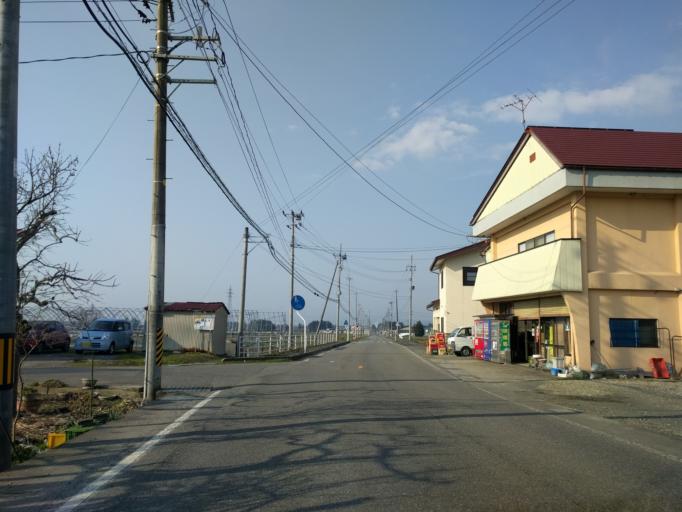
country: JP
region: Fukushima
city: Kitakata
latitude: 37.6771
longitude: 139.8950
